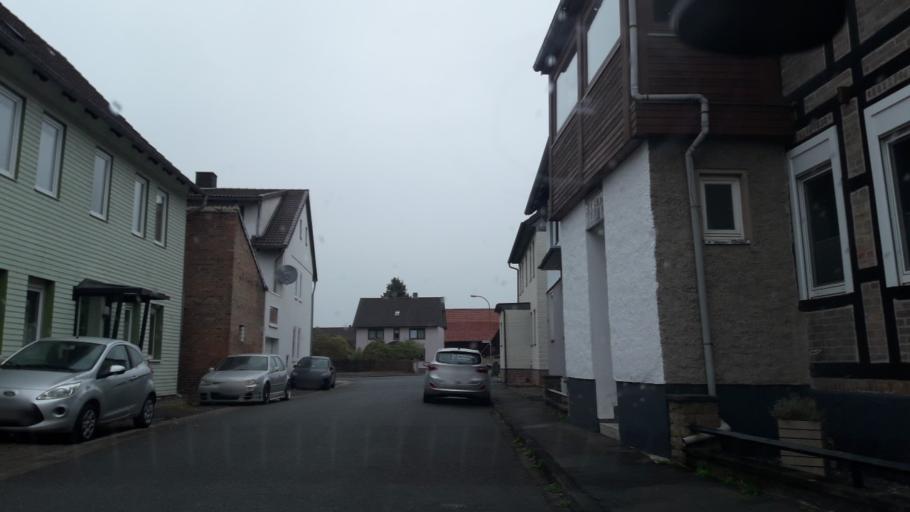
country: DE
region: Lower Saxony
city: Vienenburg
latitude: 51.9605
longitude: 10.5885
